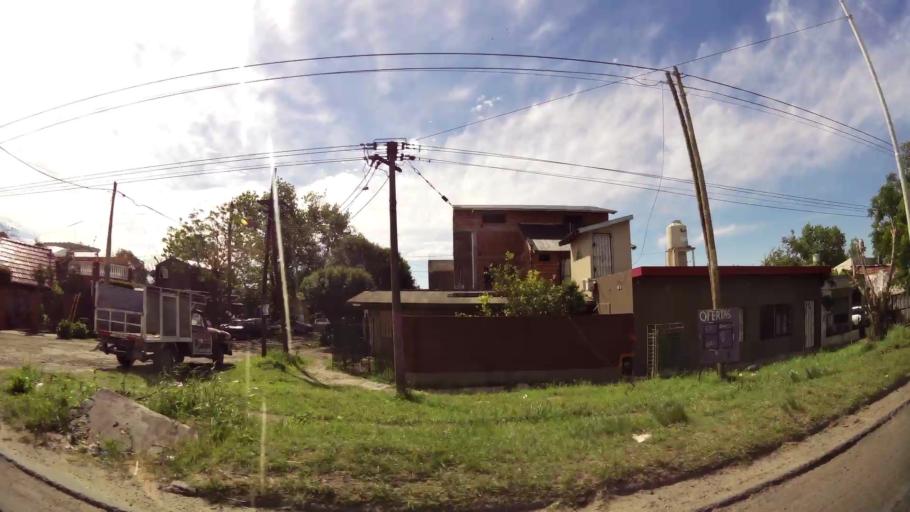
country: AR
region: Buenos Aires
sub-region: Partido de Almirante Brown
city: Adrogue
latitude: -34.7885
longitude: -58.3069
